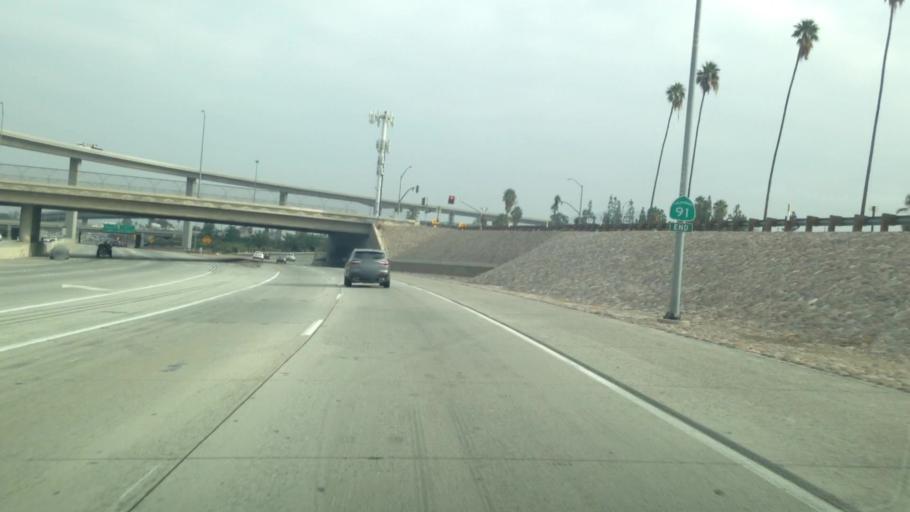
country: US
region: California
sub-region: Riverside County
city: Highgrove
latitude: 33.9898
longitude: -117.3596
